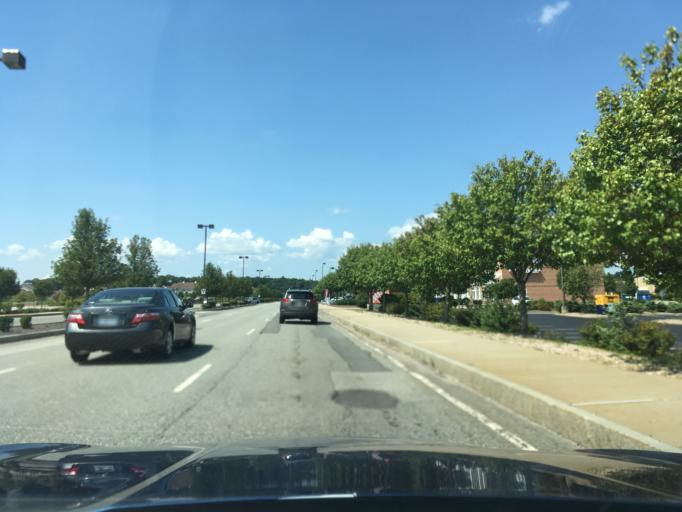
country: US
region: Rhode Island
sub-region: Kent County
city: West Warwick
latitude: 41.6616
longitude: -71.5515
